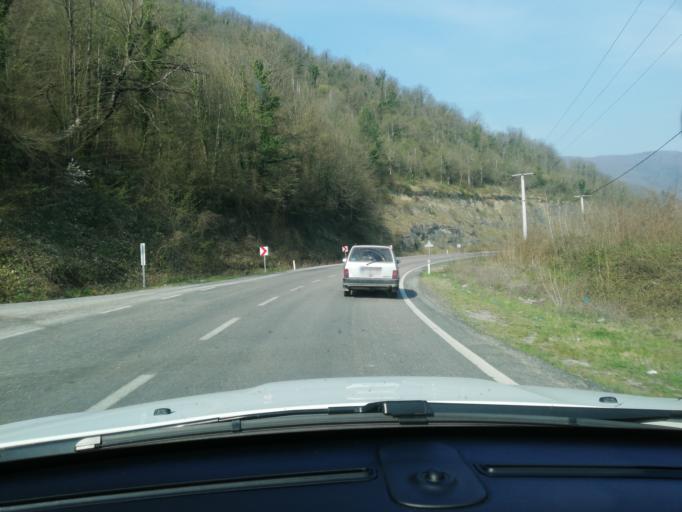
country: TR
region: Karabuk
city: Yenice
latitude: 41.2019
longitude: 32.3736
